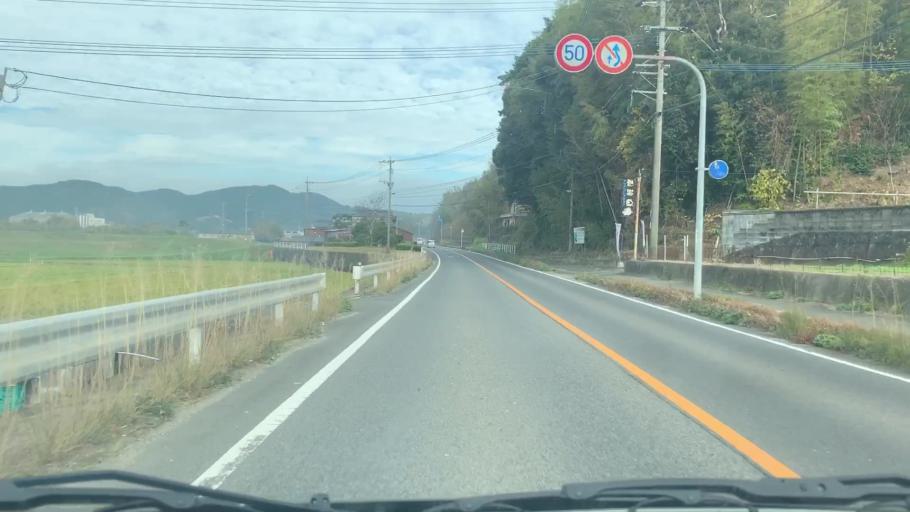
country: JP
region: Saga Prefecture
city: Karatsu
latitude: 33.3905
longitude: 129.9874
